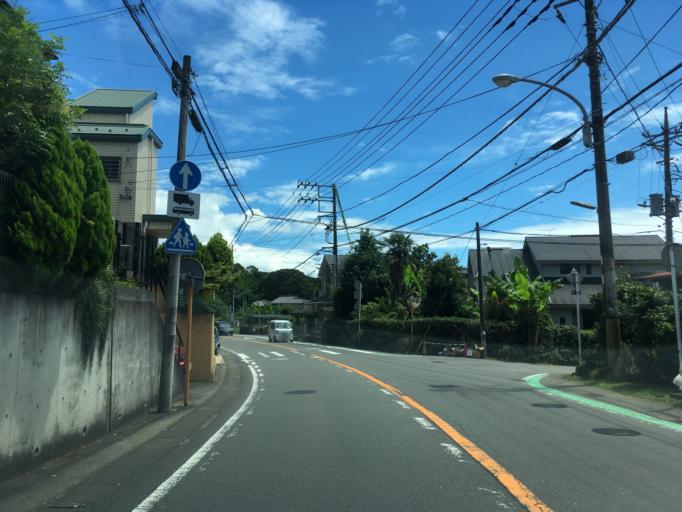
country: JP
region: Tokyo
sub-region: Machida-shi
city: Machida
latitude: 35.5608
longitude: 139.4845
